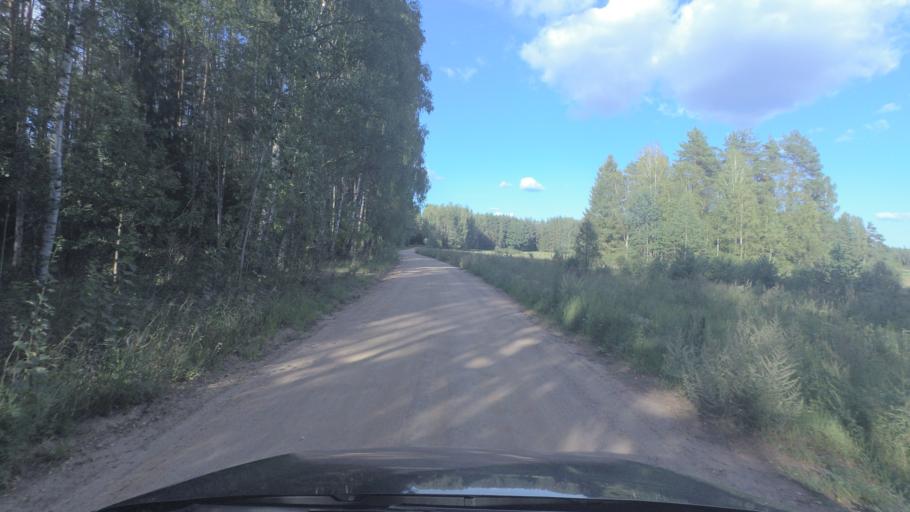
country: LT
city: Pabrade
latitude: 55.1467
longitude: 25.7471
